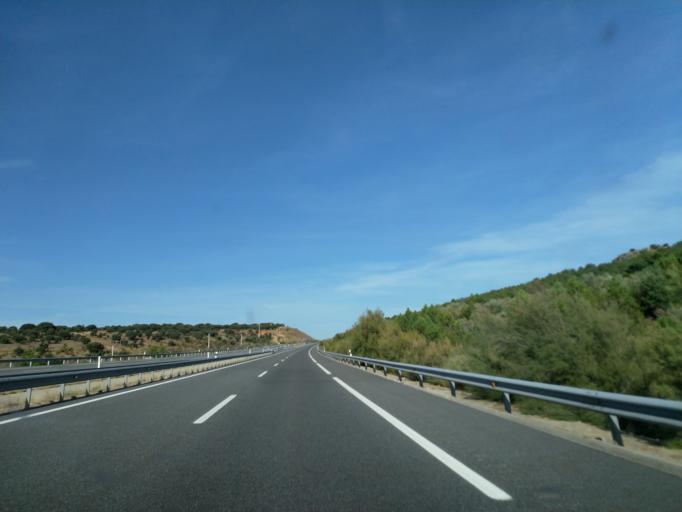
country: ES
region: Castille and Leon
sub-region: Provincia de Avila
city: Ojos-Albos
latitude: 40.7316
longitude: -4.5070
